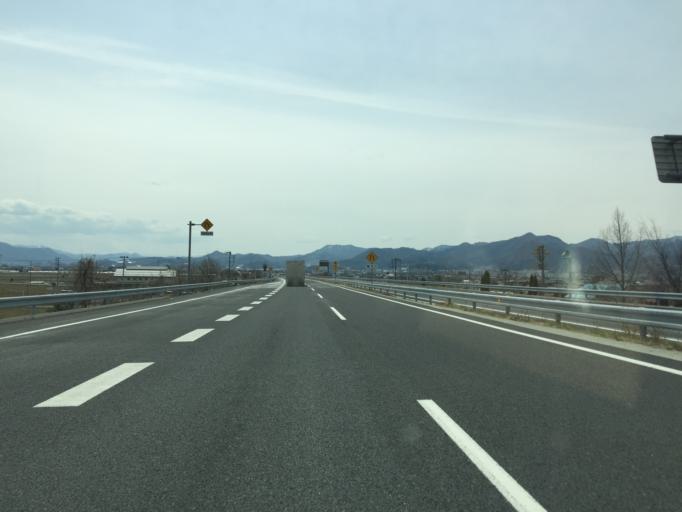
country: JP
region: Yamagata
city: Yamagata-shi
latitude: 38.2690
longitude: 140.2924
